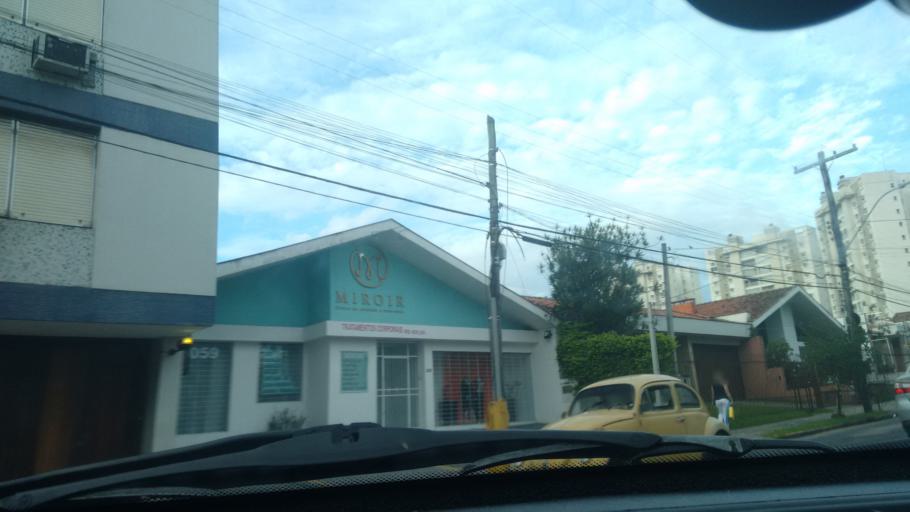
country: BR
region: Rio Grande do Sul
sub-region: Cachoeirinha
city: Cachoeirinha
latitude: -30.0060
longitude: -51.1518
